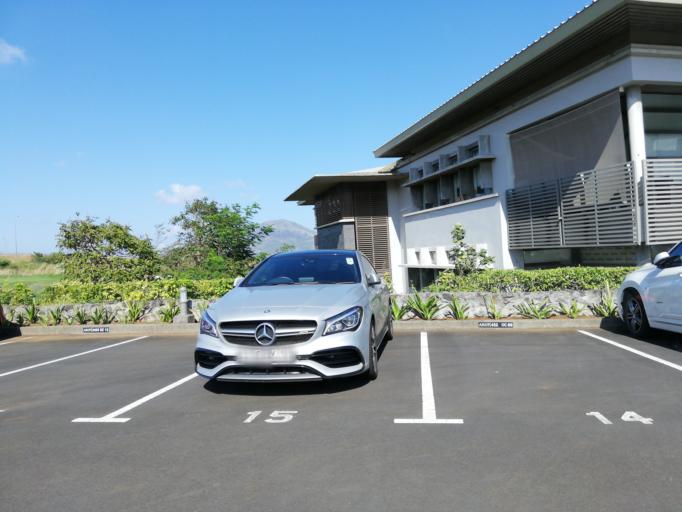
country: MU
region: Moka
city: Moka
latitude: -20.2229
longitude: 57.4929
